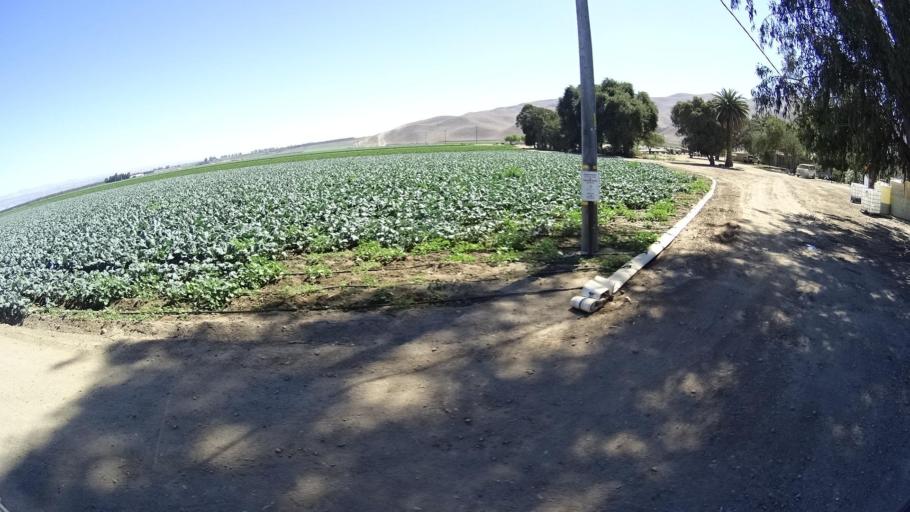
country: US
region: California
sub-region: Monterey County
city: Greenfield
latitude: 36.2973
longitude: -121.2781
